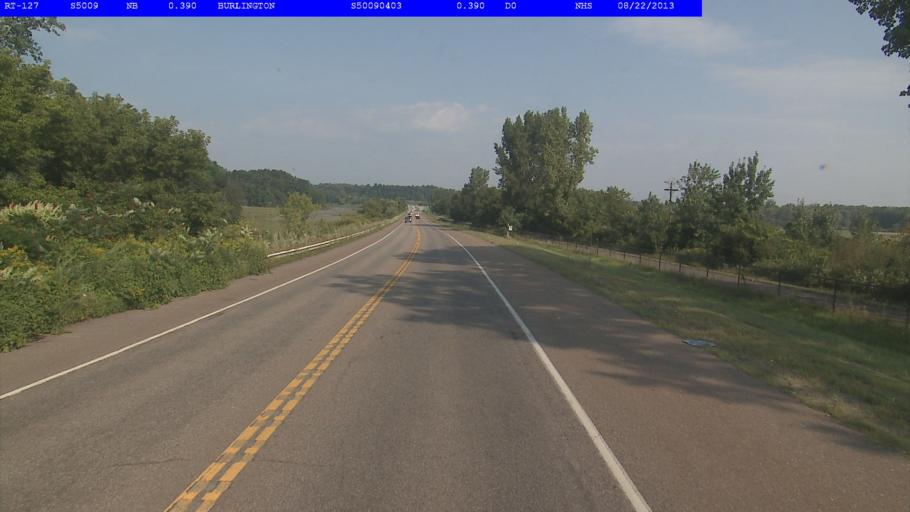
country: US
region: Vermont
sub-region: Chittenden County
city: Burlington
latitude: 44.4921
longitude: -73.2235
